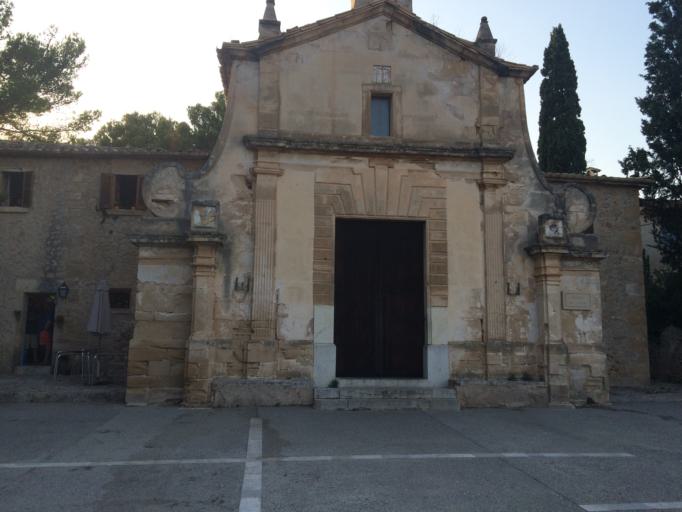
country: ES
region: Balearic Islands
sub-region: Illes Balears
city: Pollenca
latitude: 39.8802
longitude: 3.0121
